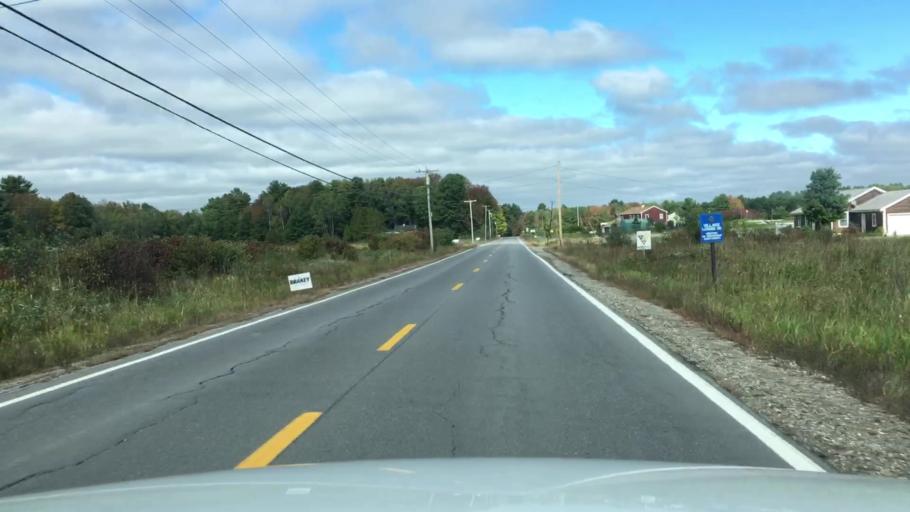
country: US
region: Maine
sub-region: Sagadahoc County
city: North Bath
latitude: 43.9981
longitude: -69.8901
